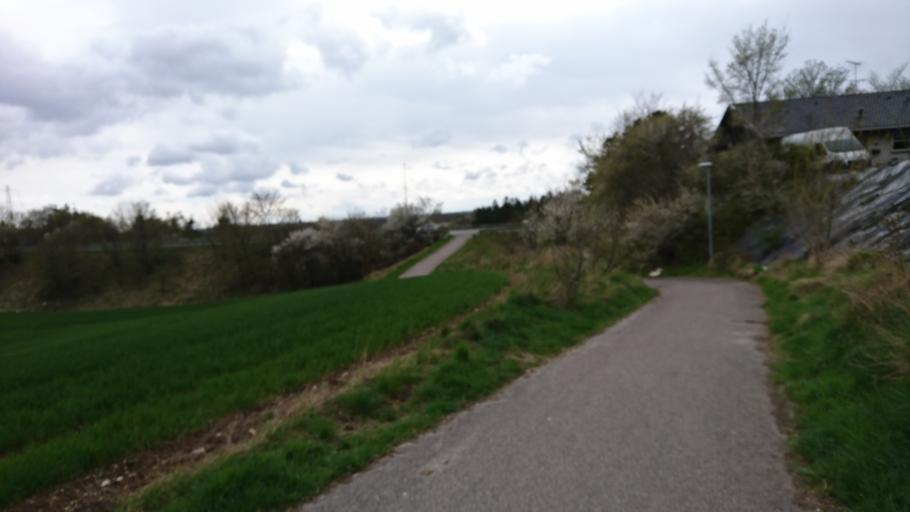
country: DK
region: Capital Region
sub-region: Egedal Kommune
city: Stenlose
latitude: 55.7670
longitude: 12.2090
